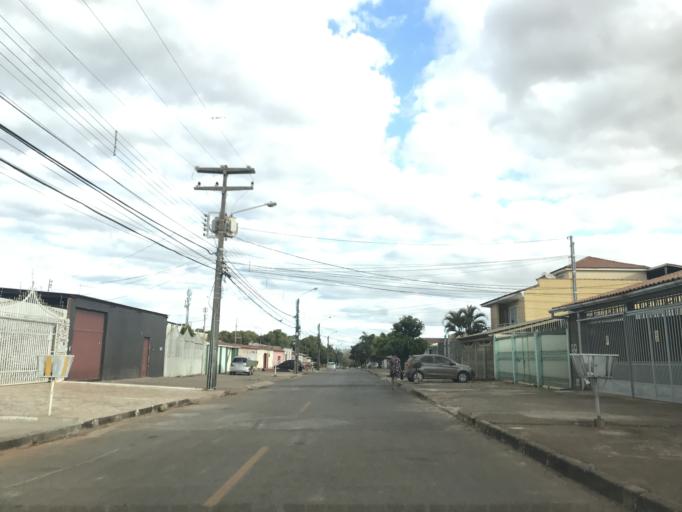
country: BR
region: Federal District
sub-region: Brasilia
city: Brasilia
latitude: -15.8014
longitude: -48.0595
